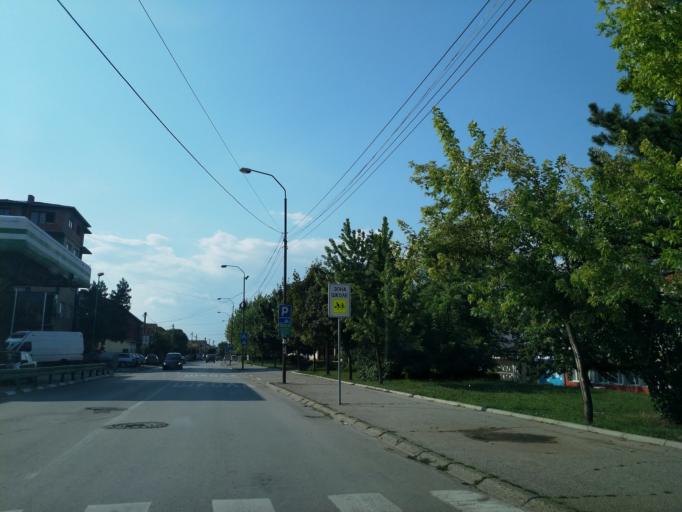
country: RS
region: Central Serbia
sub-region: Pomoravski Okrug
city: Paracin
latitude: 43.8600
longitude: 21.4075
